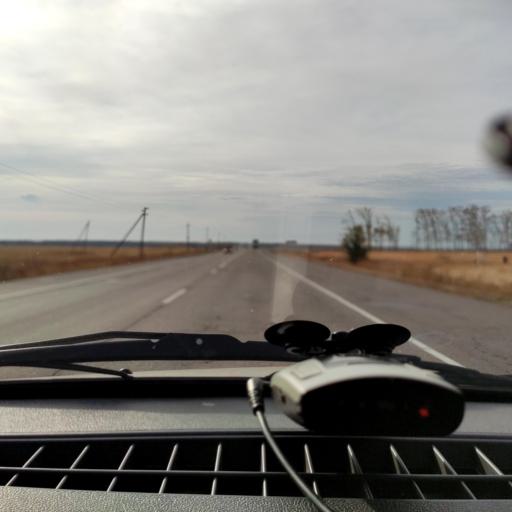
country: RU
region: Voronezj
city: Strelitsa
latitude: 51.5340
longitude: 38.9698
